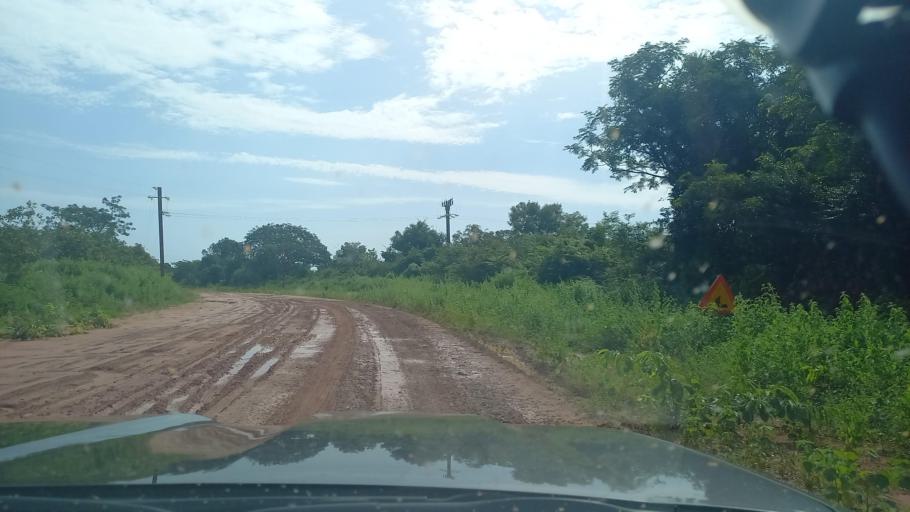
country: SN
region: Ziguinchor
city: Ziguinchor
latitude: 12.6715
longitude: -16.2149
